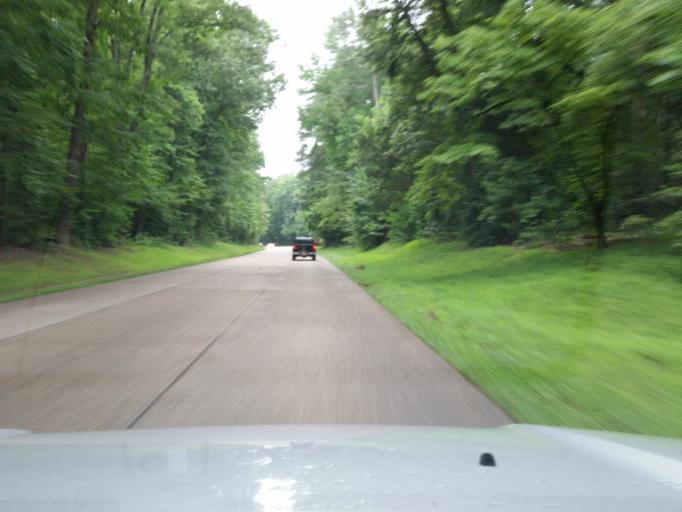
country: US
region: Virginia
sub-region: City of Williamsburg
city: Williamsburg
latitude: 37.2797
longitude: -76.6215
